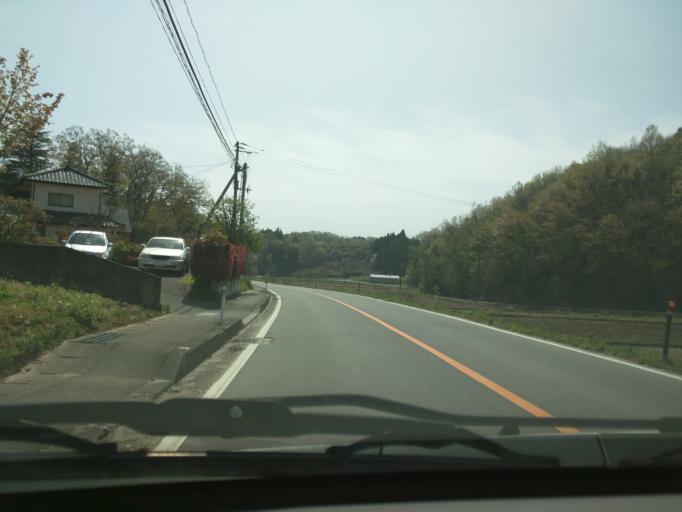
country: JP
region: Fukushima
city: Nihommatsu
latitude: 37.5724
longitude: 140.4717
